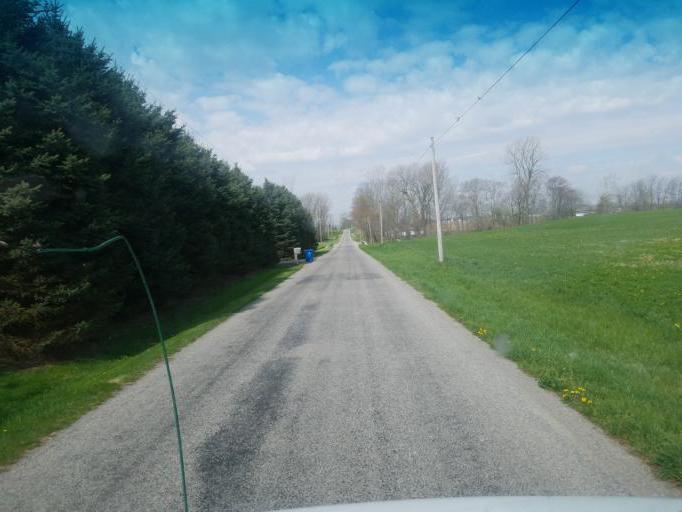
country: US
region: Ohio
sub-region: Logan County
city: Northwood
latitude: 40.4910
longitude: -83.7331
